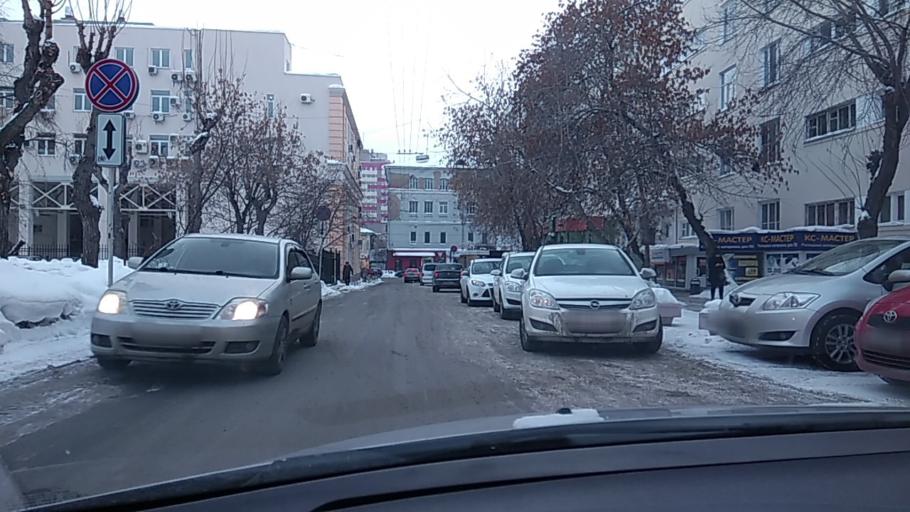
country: RU
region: Sverdlovsk
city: Yekaterinburg
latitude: 56.8348
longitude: 60.5972
